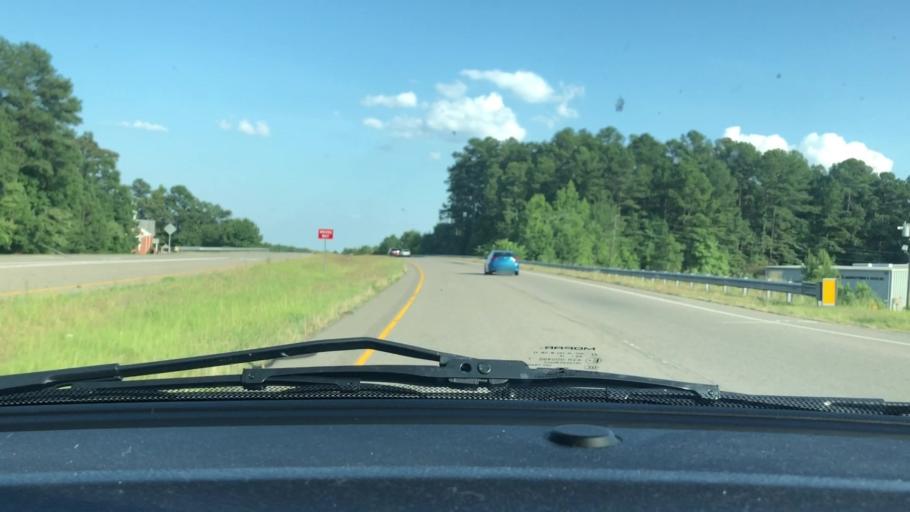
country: US
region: North Carolina
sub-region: Chatham County
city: Farmville
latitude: 35.5603
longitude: -79.2944
